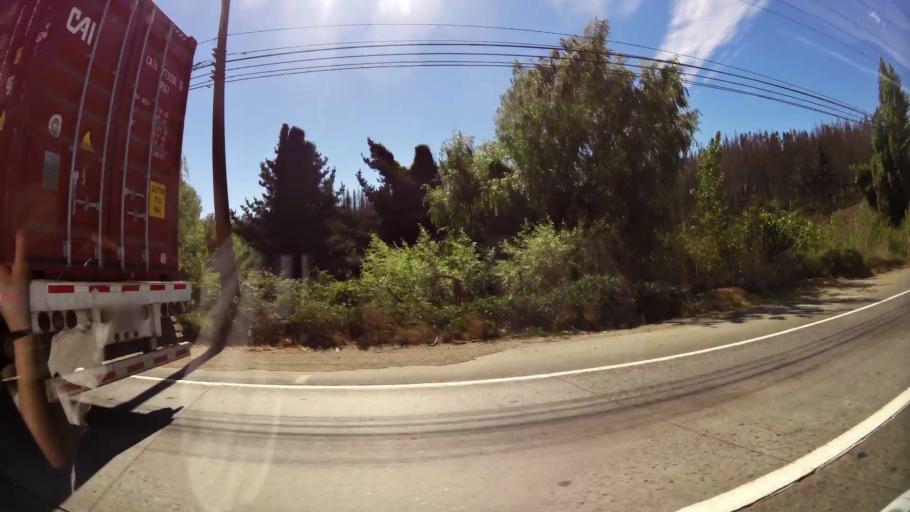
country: CL
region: Biobio
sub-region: Provincia de Concepcion
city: Penco
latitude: -36.7644
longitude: -73.0099
